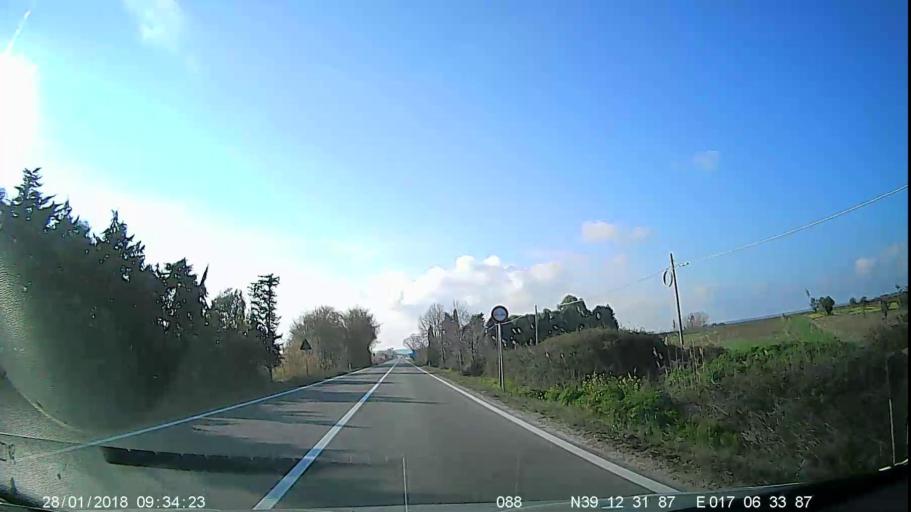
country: IT
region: Calabria
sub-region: Provincia di Crotone
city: Tronca
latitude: 39.2083
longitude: 17.1091
